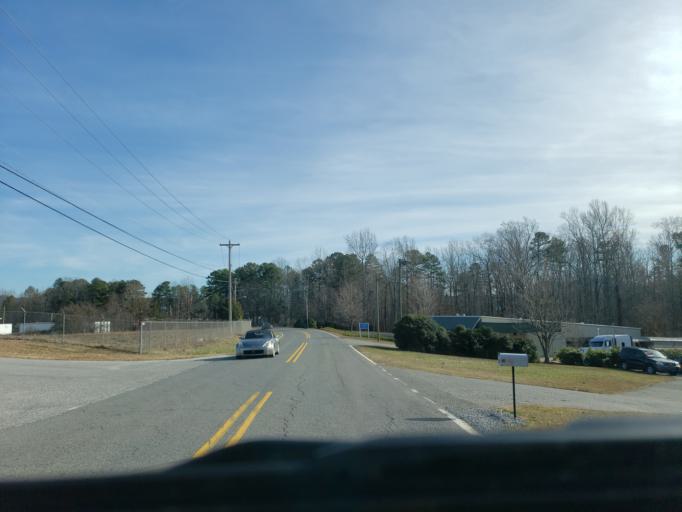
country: US
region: North Carolina
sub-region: Cleveland County
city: Kings Mountain
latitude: 35.2387
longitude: -81.3225
